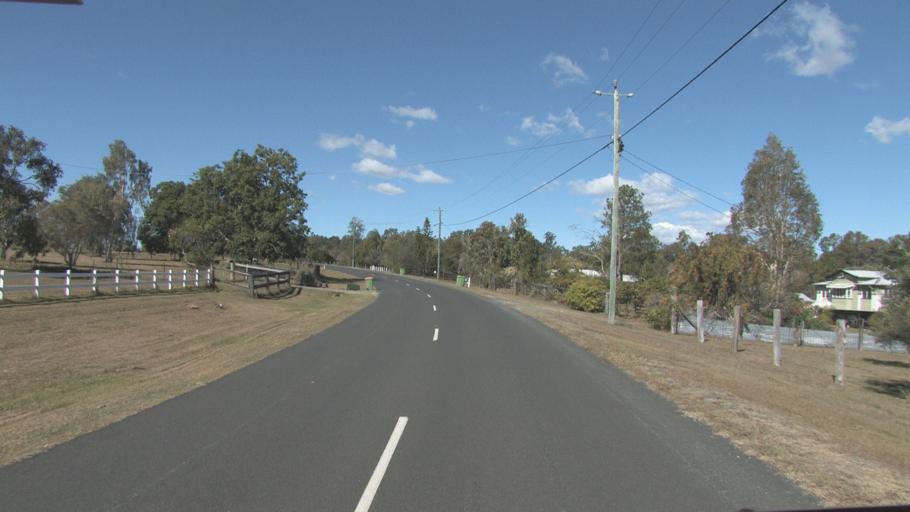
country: AU
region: Queensland
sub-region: Logan
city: North Maclean
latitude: -27.7416
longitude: 152.9465
